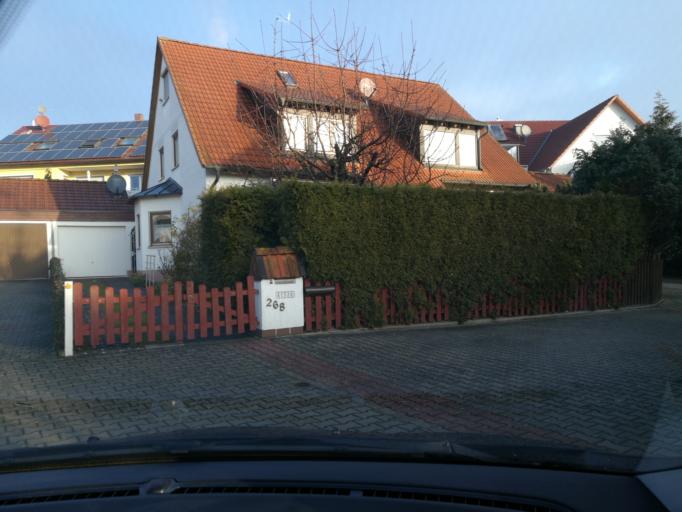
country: DE
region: Bavaria
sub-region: Regierungsbezirk Mittelfranken
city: Furth
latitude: 49.4897
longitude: 10.9477
